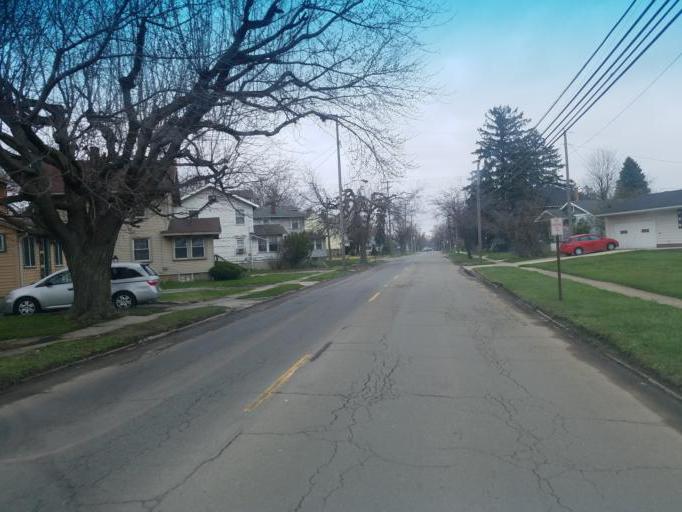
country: US
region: Ohio
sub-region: Marion County
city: Marion
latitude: 40.5724
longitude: -83.1340
